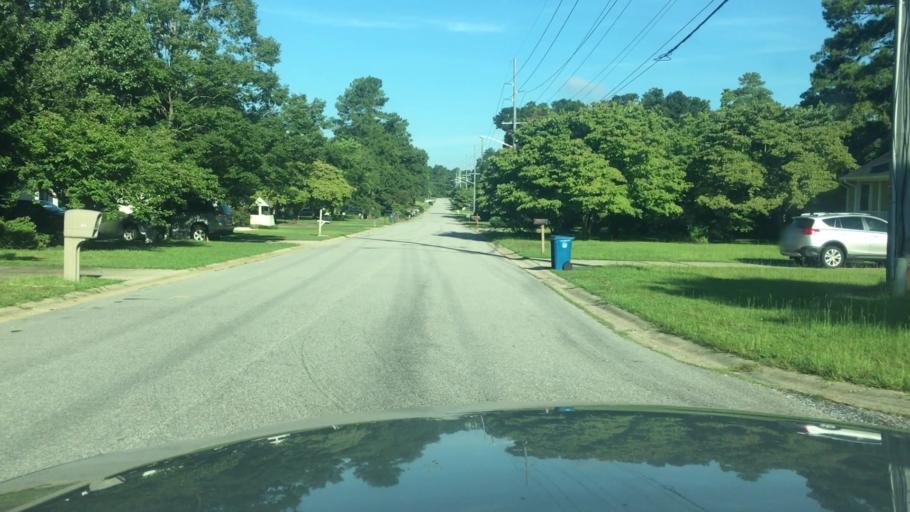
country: US
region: North Carolina
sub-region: Cumberland County
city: Fayetteville
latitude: 35.1298
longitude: -78.8855
